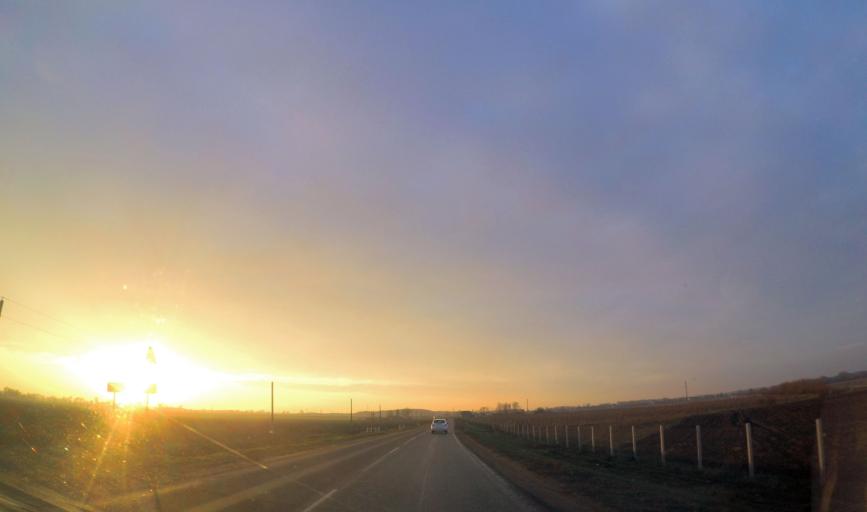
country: BY
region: Grodnenskaya
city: Hrodna
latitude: 53.7337
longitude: 23.9236
